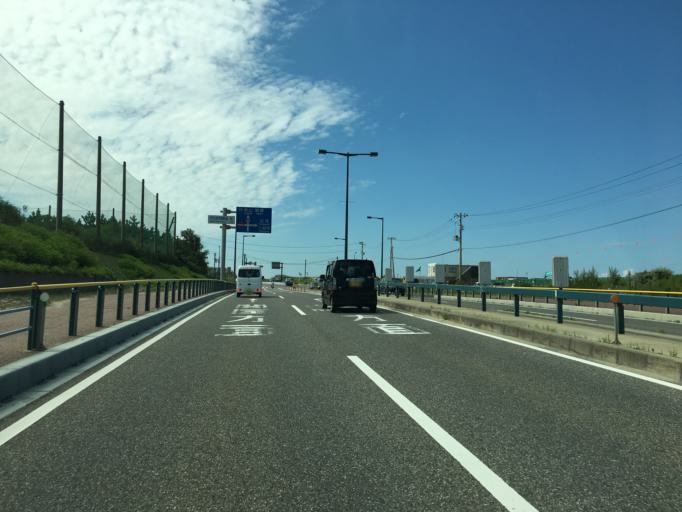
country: JP
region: Niigata
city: Niigata-shi
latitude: 37.9413
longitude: 139.0561
